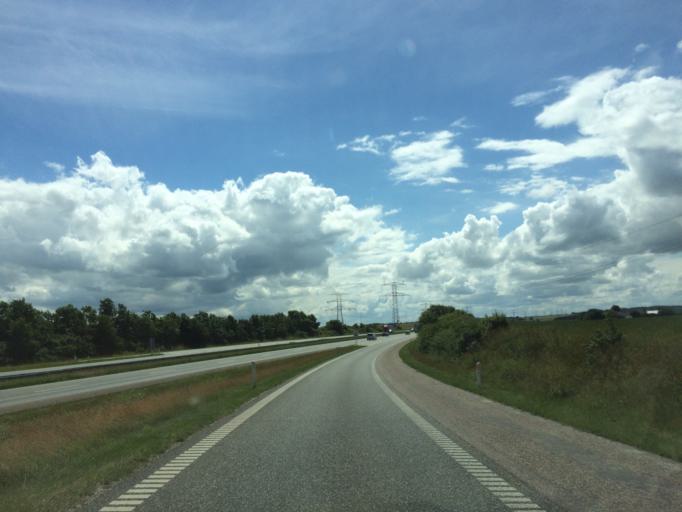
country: DK
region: North Denmark
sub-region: Rebild Kommune
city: Stovring
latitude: 56.8790
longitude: 9.8016
